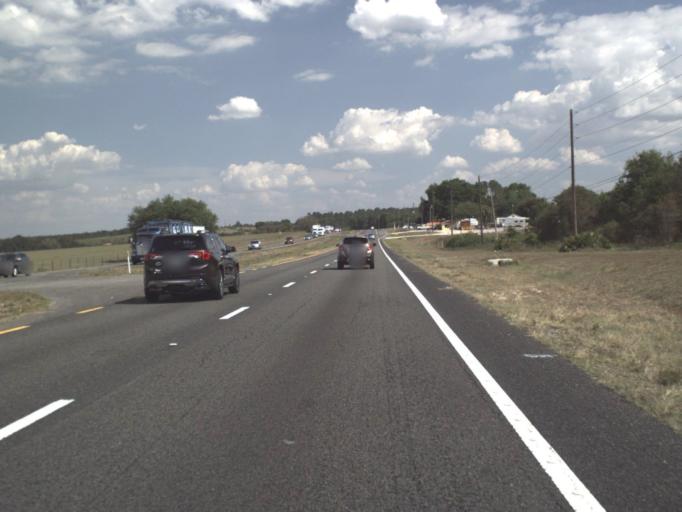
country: US
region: Florida
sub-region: Lake County
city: Mascotte
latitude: 28.6520
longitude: -81.8382
